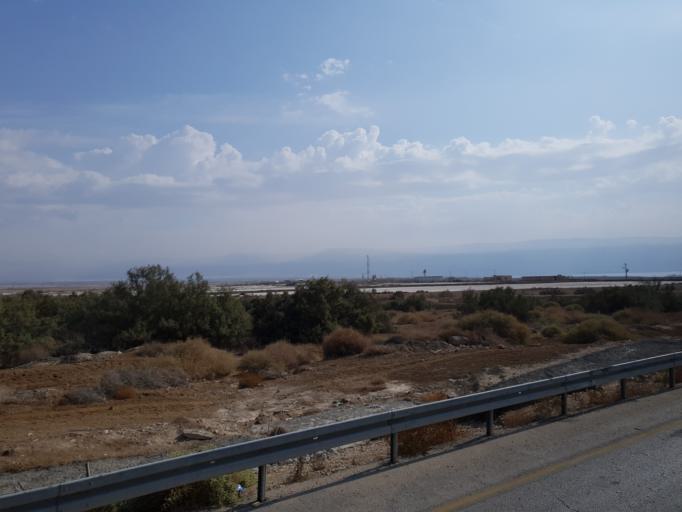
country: PS
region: West Bank
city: Jericho
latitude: 31.7767
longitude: 35.5041
